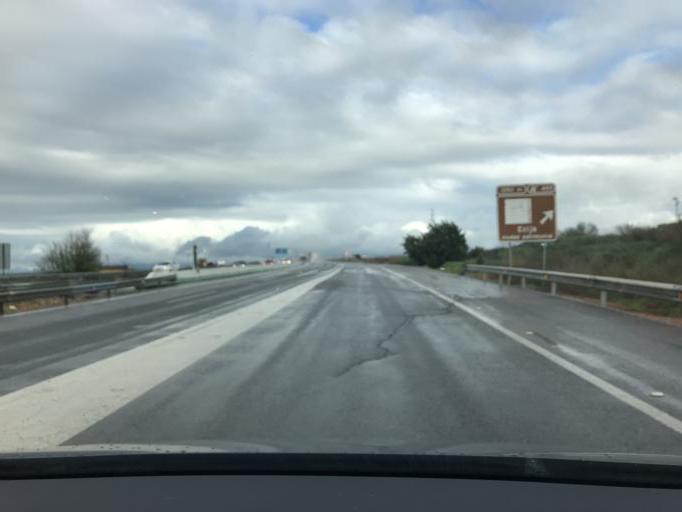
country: ES
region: Andalusia
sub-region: Provincia de Sevilla
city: Ecija
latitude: 37.5259
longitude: -5.1090
